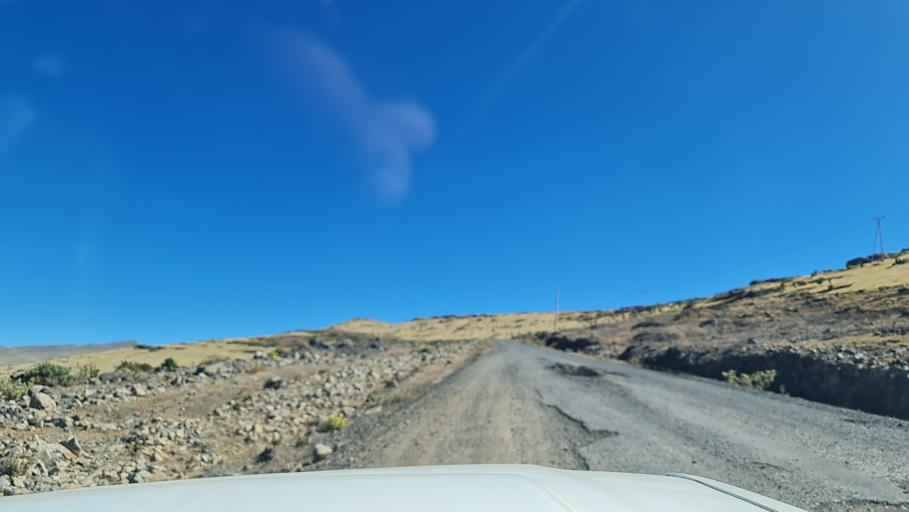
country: ET
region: Amhara
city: Debark'
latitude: 13.1606
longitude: 38.1915
